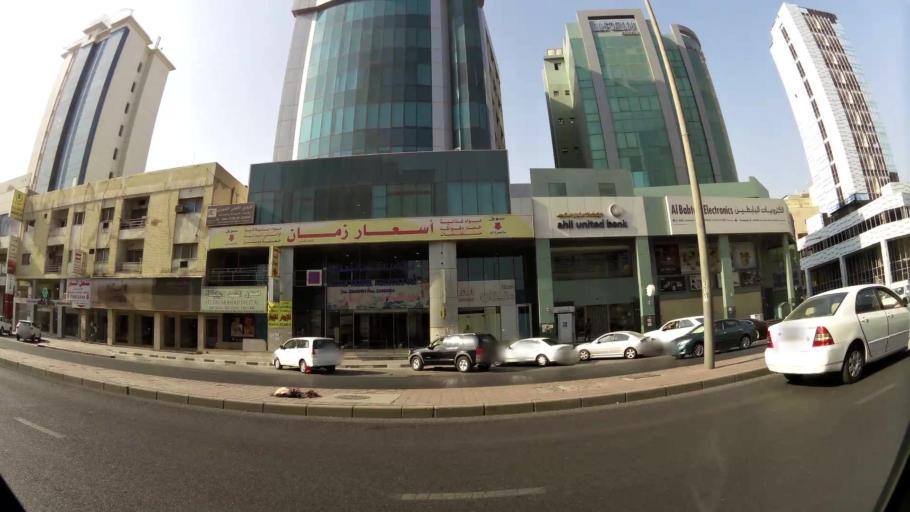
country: KW
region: Muhafazat Hawalli
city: Hawalli
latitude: 29.3418
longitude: 48.0193
